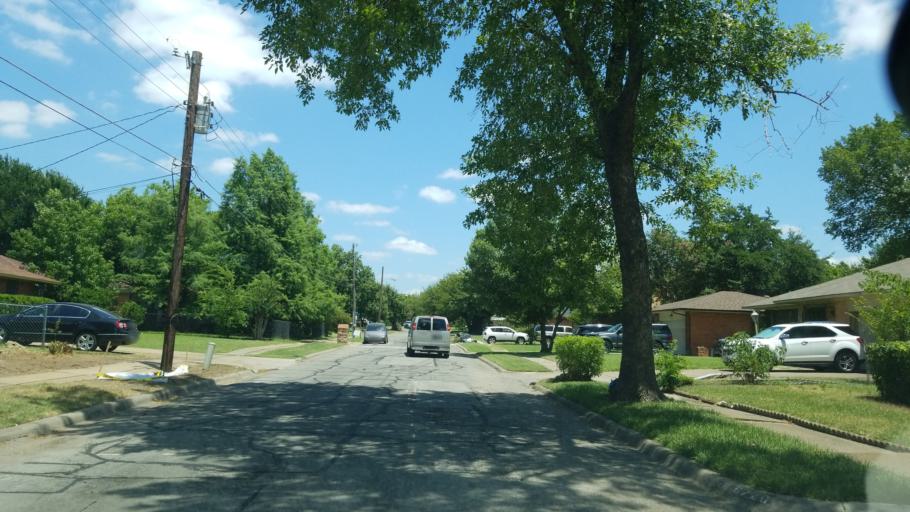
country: US
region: Texas
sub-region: Dallas County
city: Balch Springs
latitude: 32.7389
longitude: -96.7059
